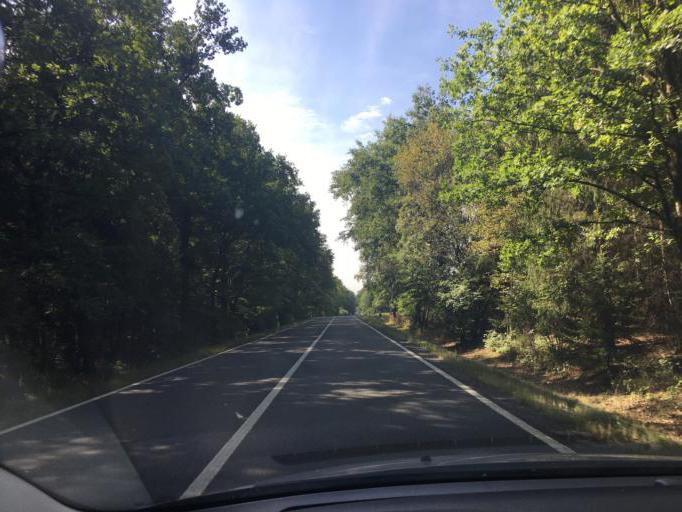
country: DE
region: Thuringia
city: Auma
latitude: 50.7236
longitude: 11.9075
